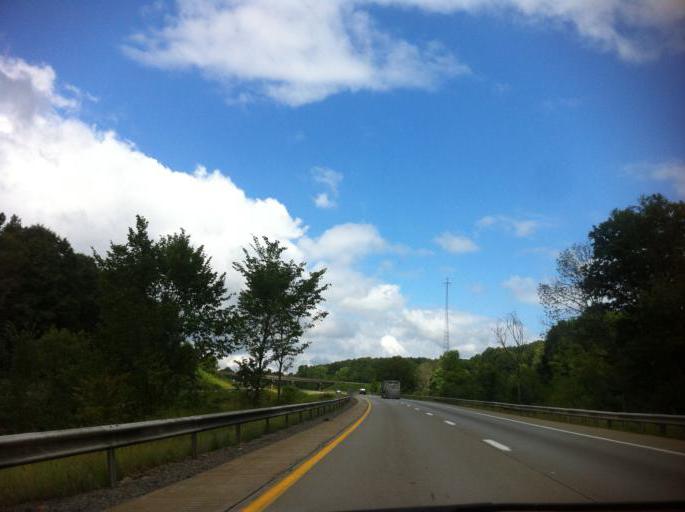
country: US
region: Pennsylvania
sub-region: Lawrence County
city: New Wilmington
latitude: 41.1837
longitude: -80.3226
